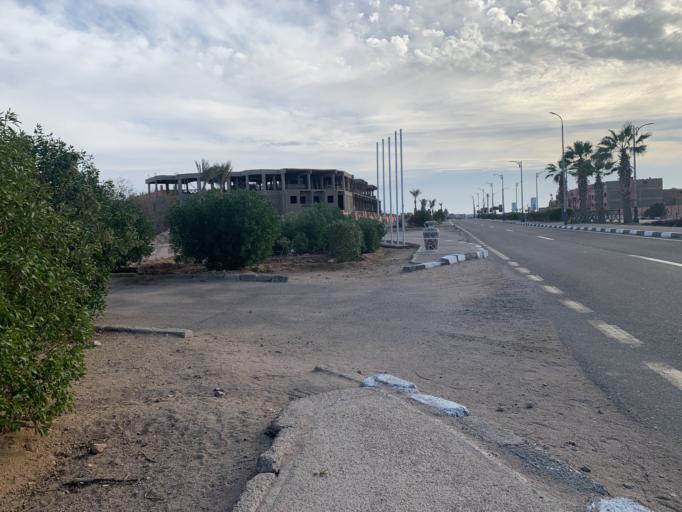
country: EG
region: South Sinai
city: Sharm el-Sheikh
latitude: 28.0180
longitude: 34.4346
